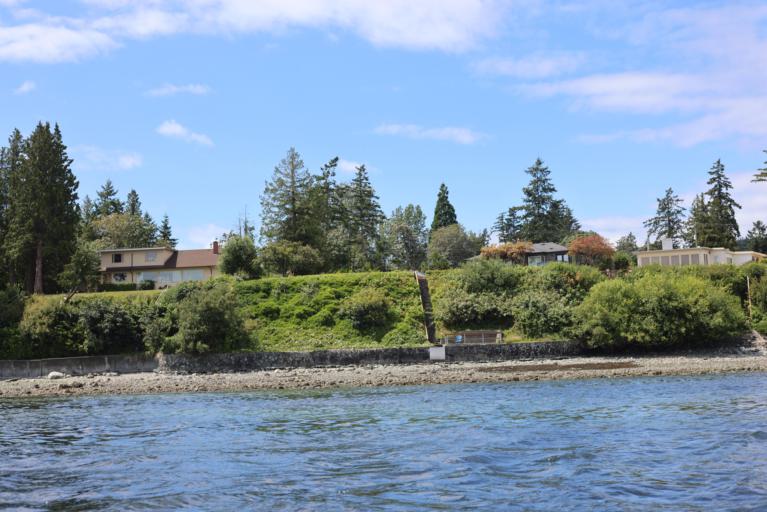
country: CA
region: British Columbia
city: North Saanich
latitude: 48.6132
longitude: -123.3974
